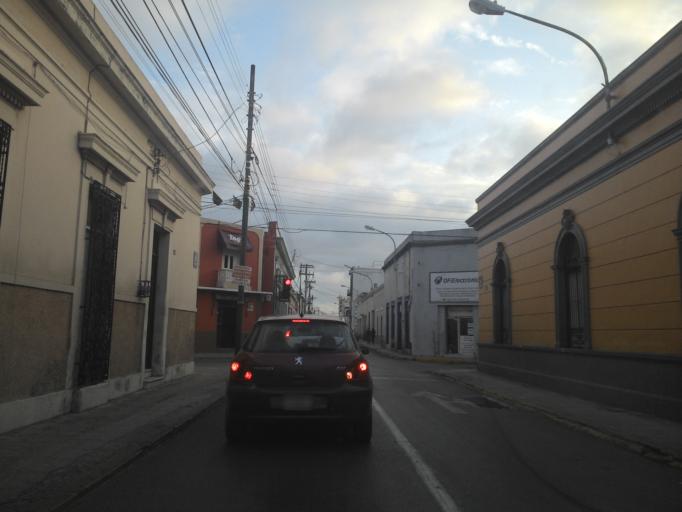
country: MX
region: Yucatan
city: Merida
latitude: 20.9743
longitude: -89.6204
